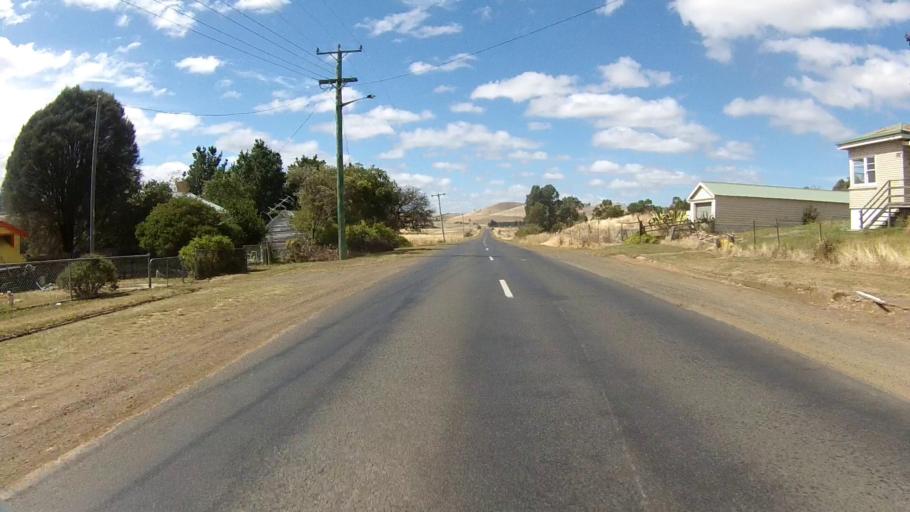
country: AU
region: Tasmania
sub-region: Brighton
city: Bridgewater
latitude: -42.5364
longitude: 147.3660
